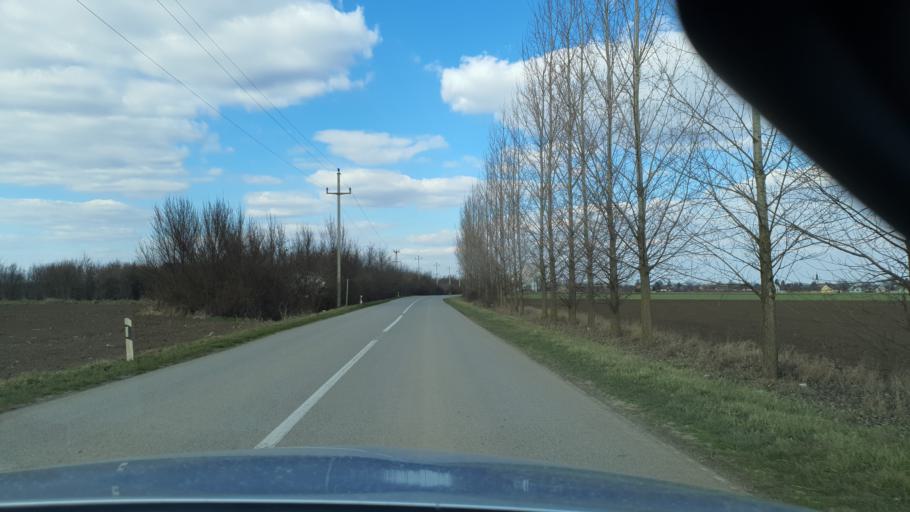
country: RS
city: Ravno Selo
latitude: 45.4407
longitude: 19.6066
